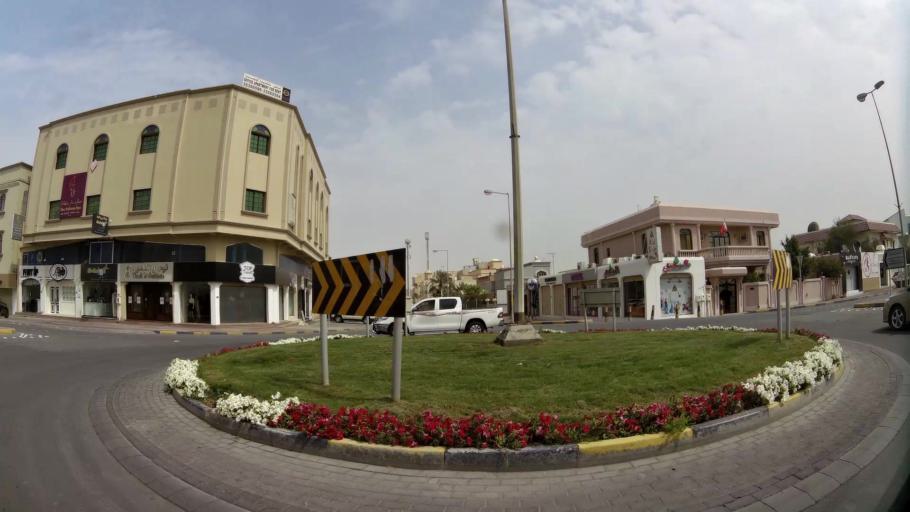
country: BH
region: Northern
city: Ar Rifa'
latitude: 26.1313
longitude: 50.5408
